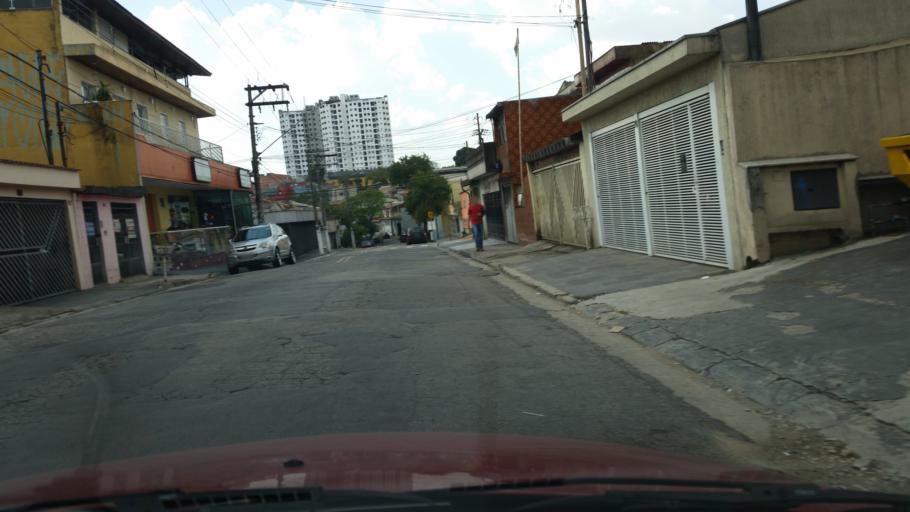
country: BR
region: Sao Paulo
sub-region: Santo Andre
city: Santo Andre
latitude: -23.6523
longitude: -46.5514
